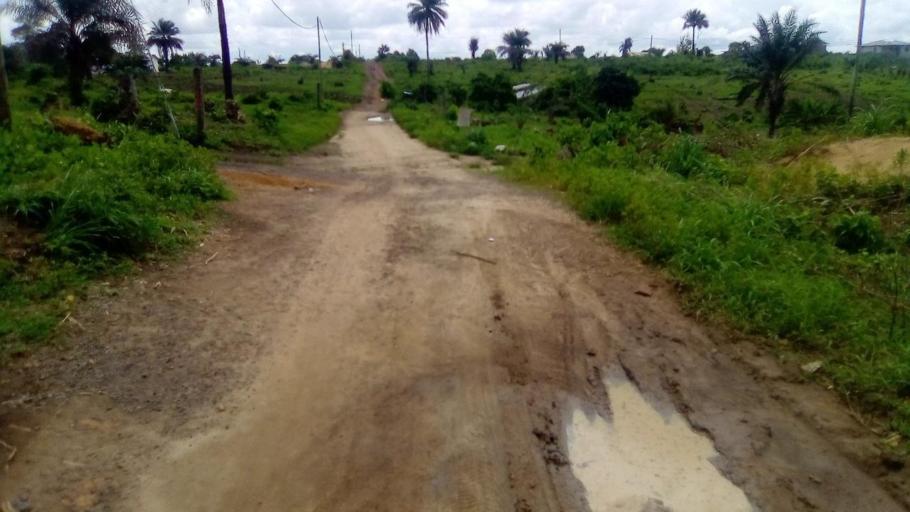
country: SL
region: Southern Province
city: Bo
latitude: 7.9324
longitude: -11.7465
